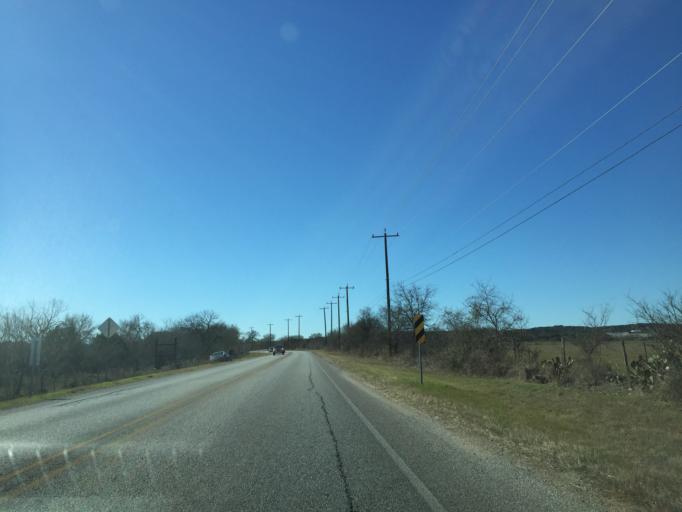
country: US
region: Texas
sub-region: Comal County
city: Bulverde
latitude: 29.7477
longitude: -98.4128
